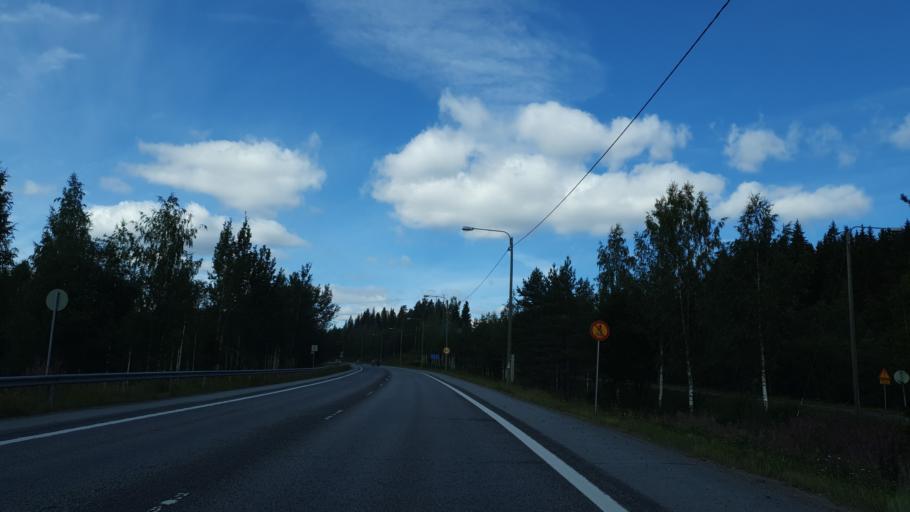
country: FI
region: Central Finland
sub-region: Jyvaeskylae
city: Muurame
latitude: 62.1657
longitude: 25.6826
